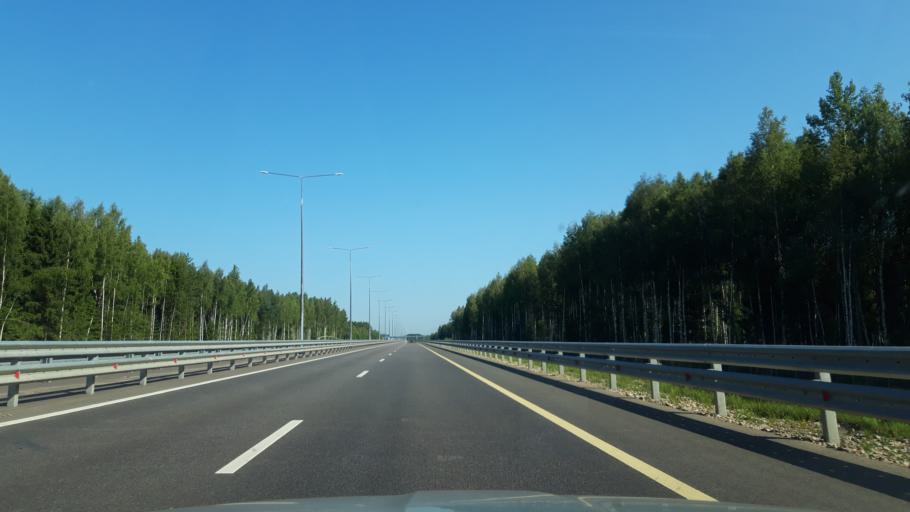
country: RU
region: Tverskaya
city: Zavidovo
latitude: 56.5371
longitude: 36.4949
